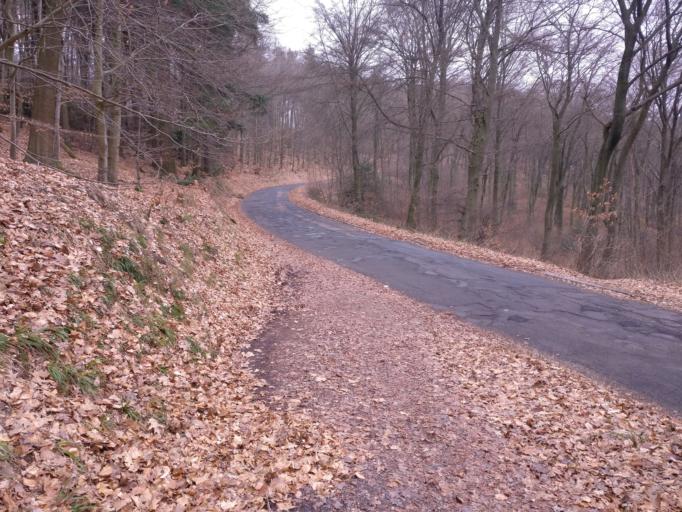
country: DE
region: Baden-Wuerttemberg
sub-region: Karlsruhe Region
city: Heidelberg
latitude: 49.4225
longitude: 8.7039
